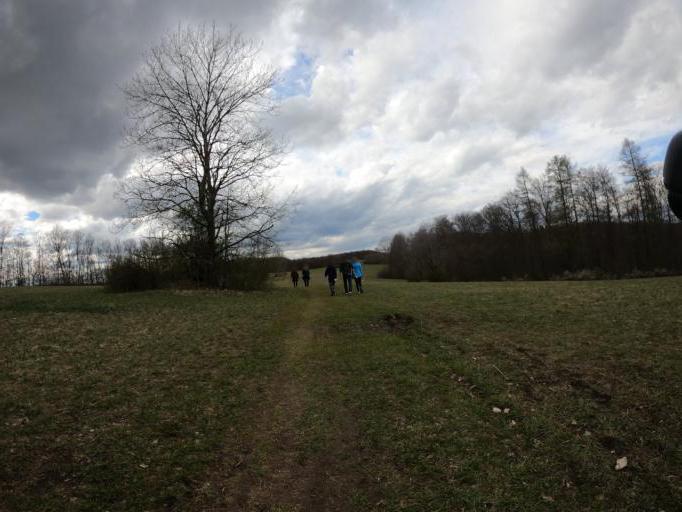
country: DE
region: Baden-Wuerttemberg
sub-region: Tuebingen Region
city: Gomaringen
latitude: 48.3974
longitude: 9.1254
